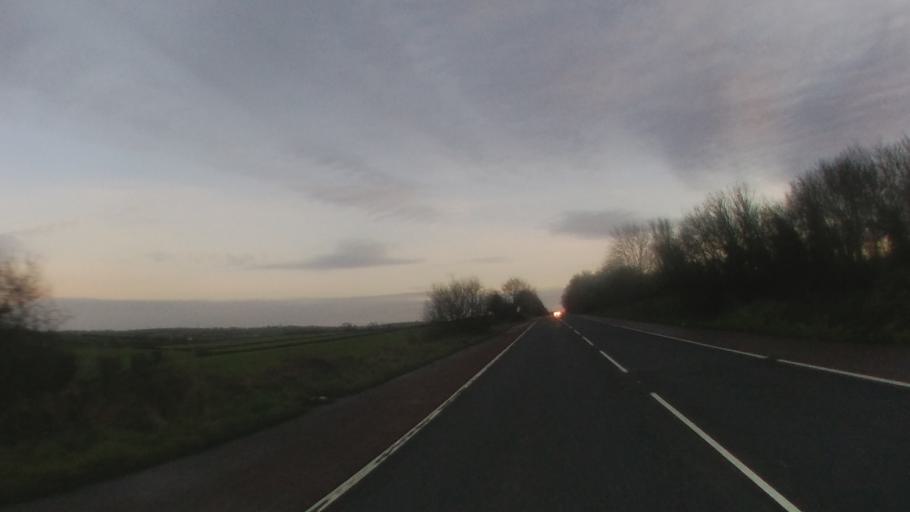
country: GB
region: Northern Ireland
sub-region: Armagh District
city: Tandragee
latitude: 54.2872
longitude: -6.4948
